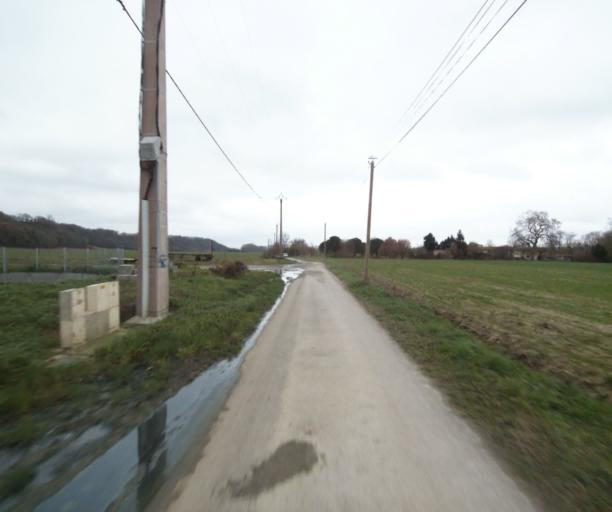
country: FR
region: Midi-Pyrenees
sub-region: Departement de l'Ariege
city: Saverdun
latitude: 43.2096
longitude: 1.5956
